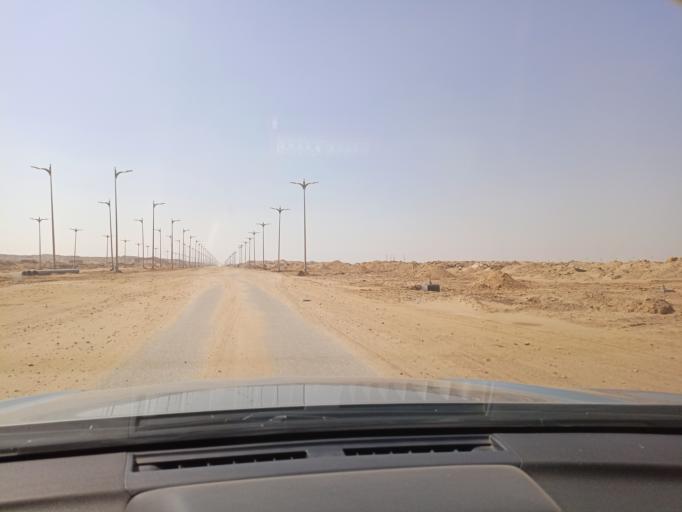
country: EG
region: Muhafazat al Qalyubiyah
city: Al Khankah
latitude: 30.0078
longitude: 31.6313
